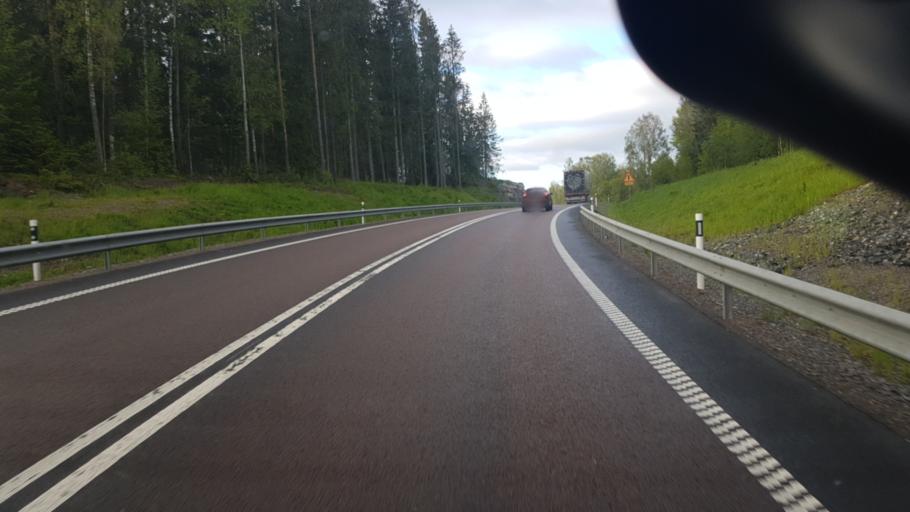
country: SE
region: Vaermland
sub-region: Eda Kommun
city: Amotfors
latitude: 59.7979
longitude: 12.3343
